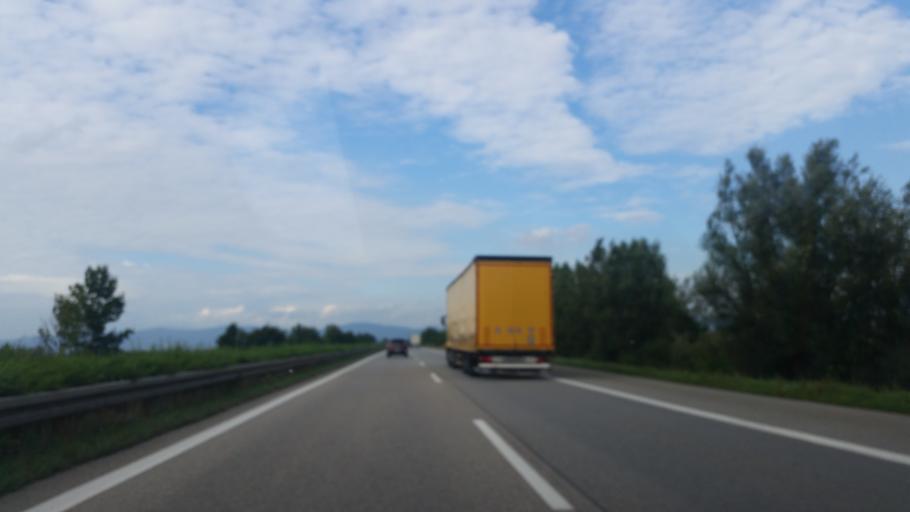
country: DE
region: Bavaria
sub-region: Lower Bavaria
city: Wallersdorf
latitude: 48.7612
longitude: 12.7714
